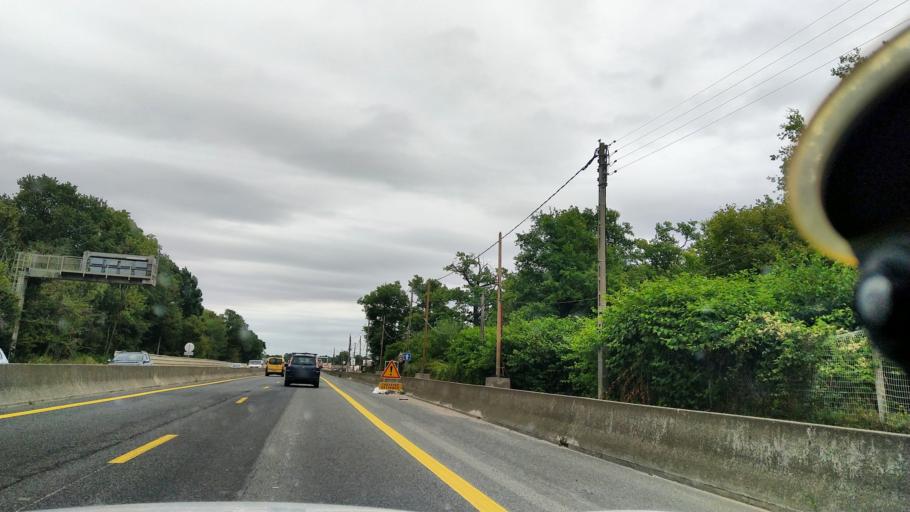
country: FR
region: Ile-de-France
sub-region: Departement de Seine-et-Marne
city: Villevaude
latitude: 48.9419
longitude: 2.6443
